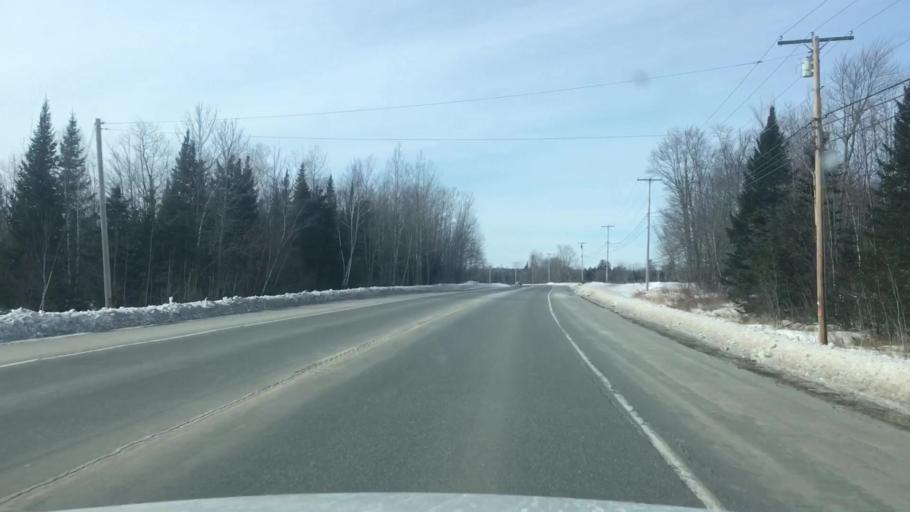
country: US
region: Maine
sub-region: Penobscot County
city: Kenduskeag
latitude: 44.9080
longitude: -68.8948
